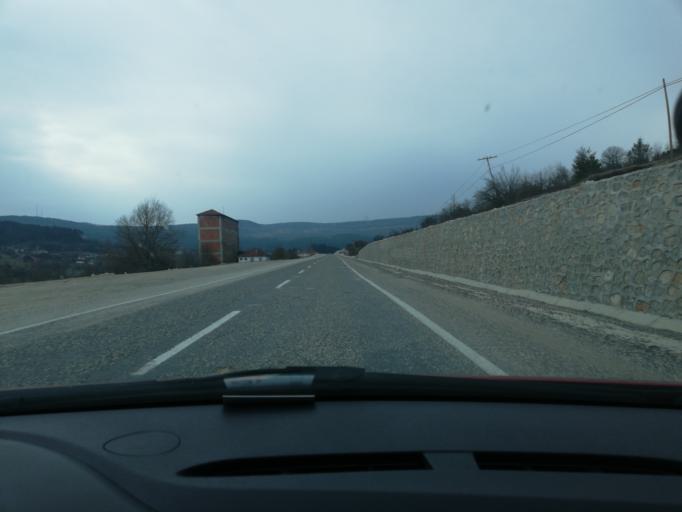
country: TR
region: Kastamonu
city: Pinarbasi
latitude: 41.5939
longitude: 33.0980
